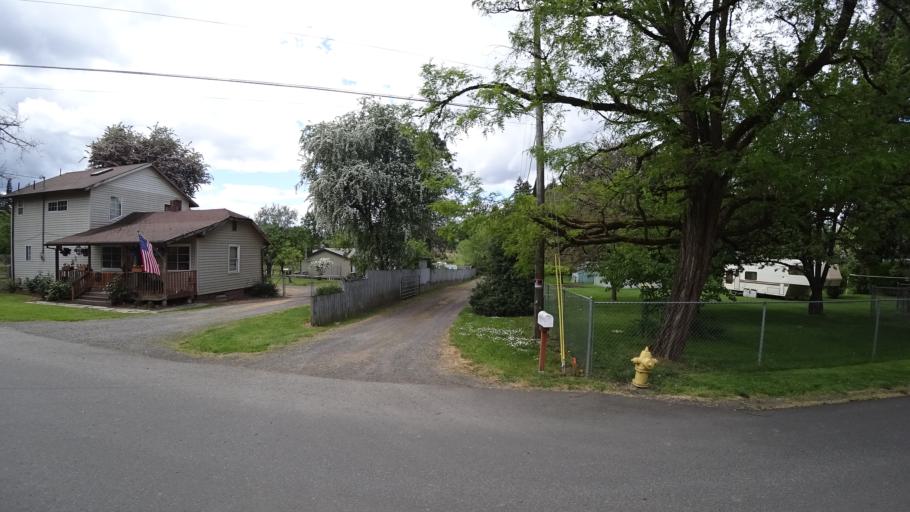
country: US
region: Oregon
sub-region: Washington County
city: Aloha
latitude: 45.4745
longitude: -122.8608
